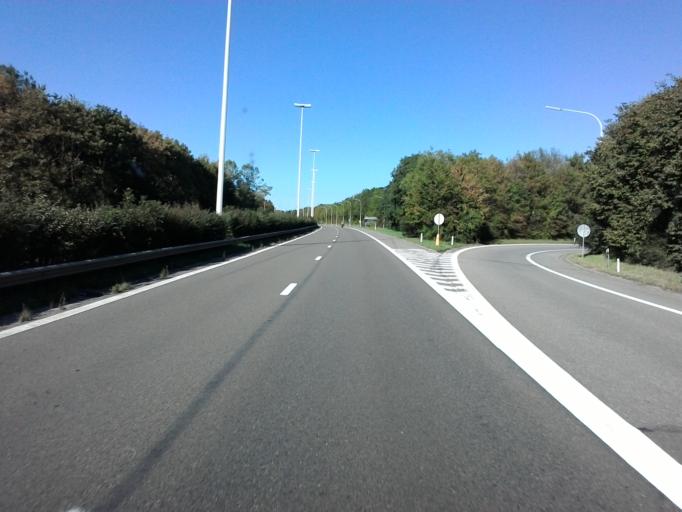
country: BE
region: Wallonia
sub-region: Province du Luxembourg
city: Aubange
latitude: 49.5640
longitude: 5.8194
